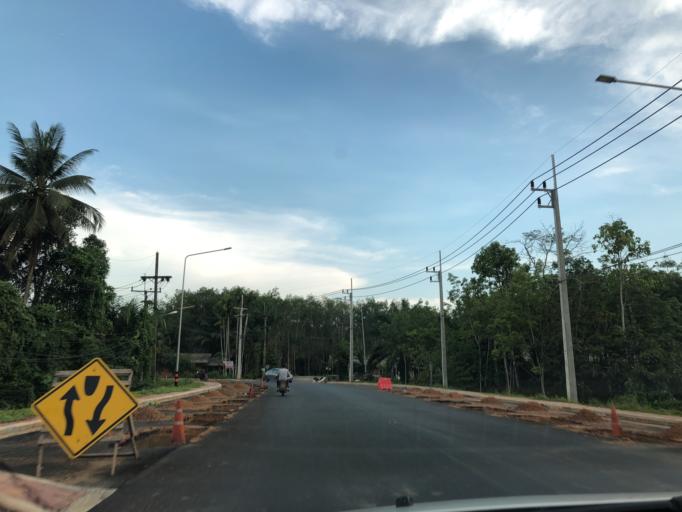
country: TH
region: Phangnga
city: Ban Ao Nang
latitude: 8.0714
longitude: 98.8376
